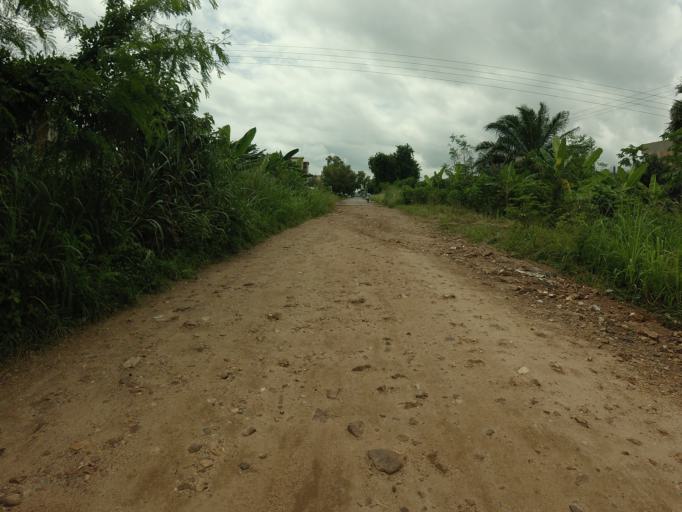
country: GH
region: Volta
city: Ho
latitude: 6.5894
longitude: 0.4606
